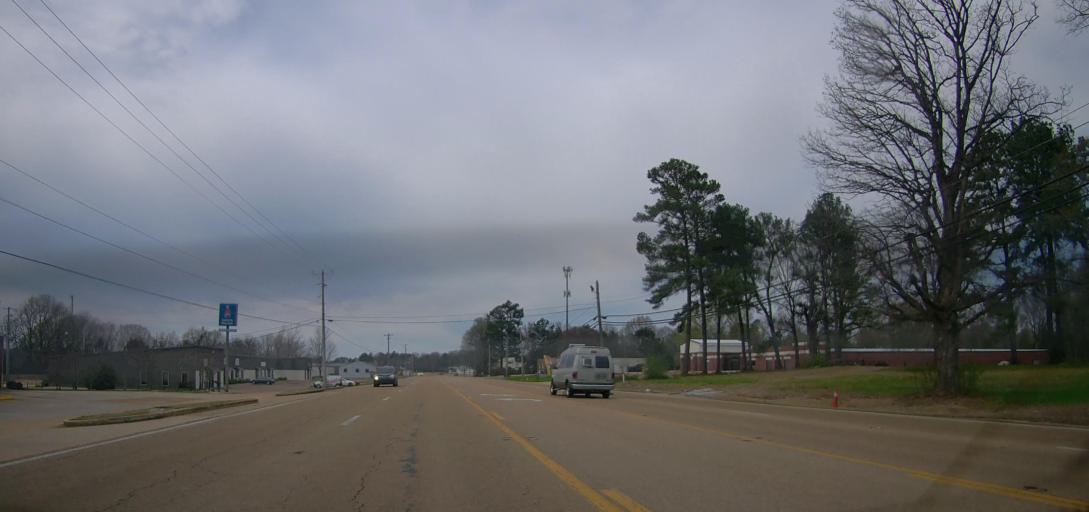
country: US
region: Mississippi
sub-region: Lee County
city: Tupelo
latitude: 34.2878
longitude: -88.7434
